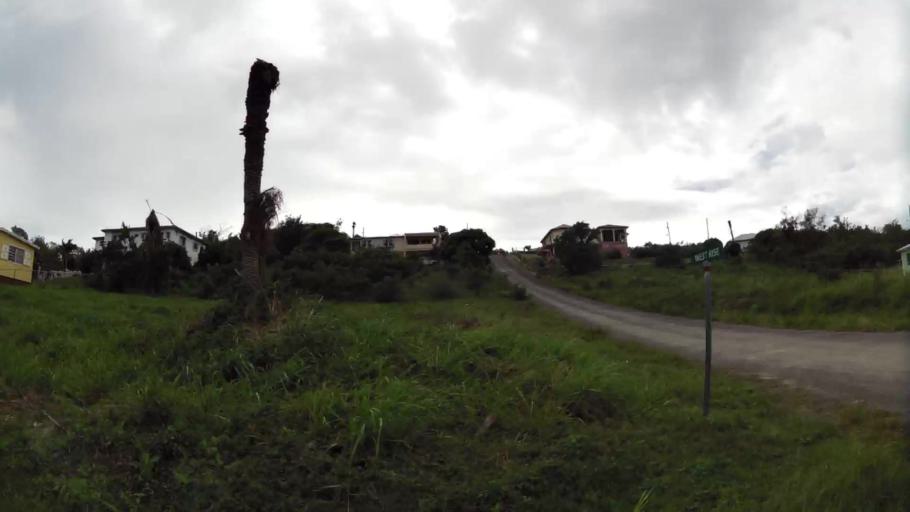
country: AG
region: Saint John
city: Potters Village
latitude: 17.0889
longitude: -61.8089
